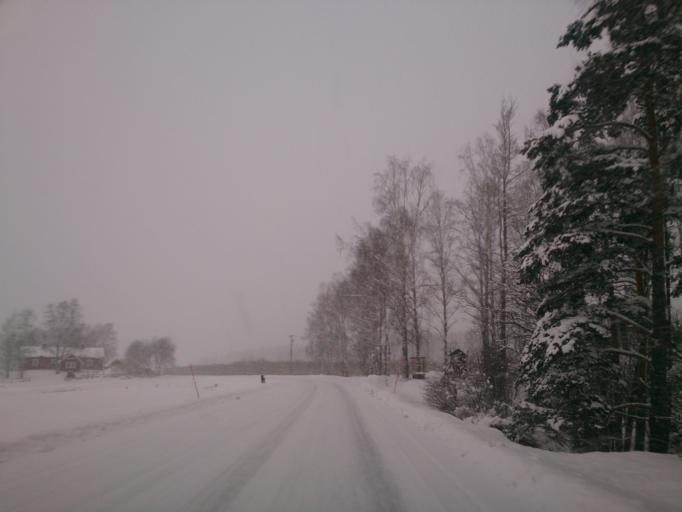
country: SE
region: OEstergoetland
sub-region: Norrkopings Kommun
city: Kimstad
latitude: 58.3939
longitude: 15.9672
